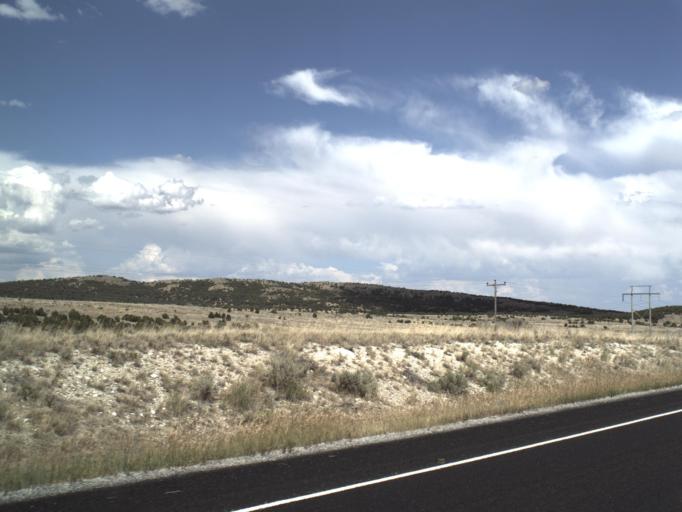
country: US
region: Idaho
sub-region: Minidoka County
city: Rupert
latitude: 41.9868
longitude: -113.1778
